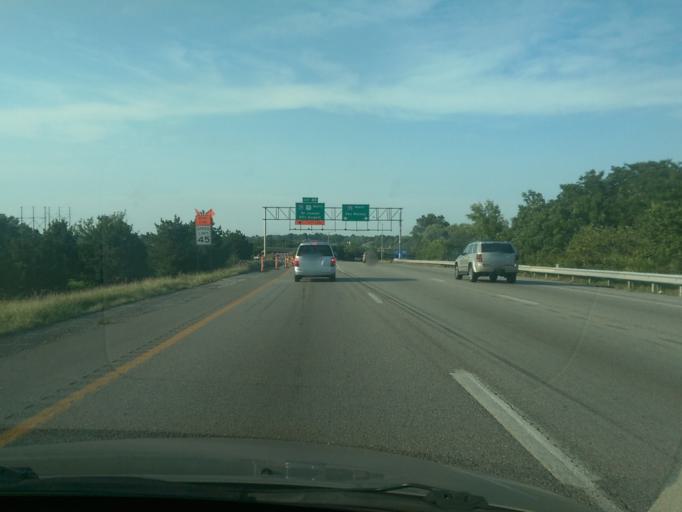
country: US
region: Missouri
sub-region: Clay County
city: North Kansas City
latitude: 39.1668
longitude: -94.5585
